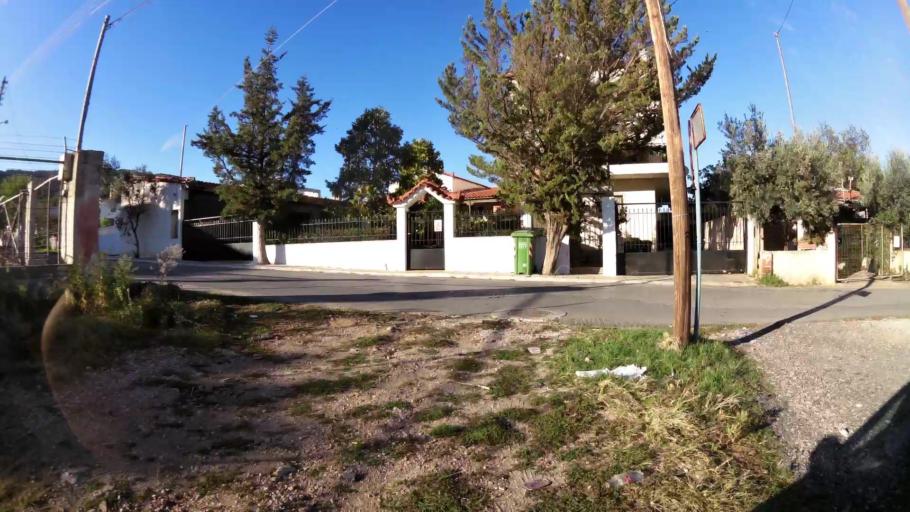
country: GR
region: Attica
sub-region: Nomarchia Anatolikis Attikis
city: Paiania
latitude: 37.9667
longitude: 23.8474
